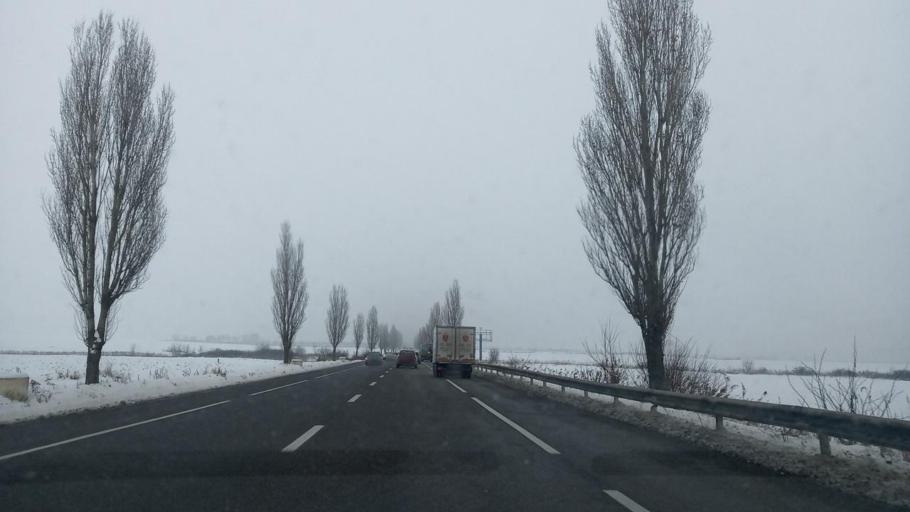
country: RO
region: Bacau
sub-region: Comuna Nicolae Balcescu
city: Nicolae Balcescu
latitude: 46.4554
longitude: 26.9144
